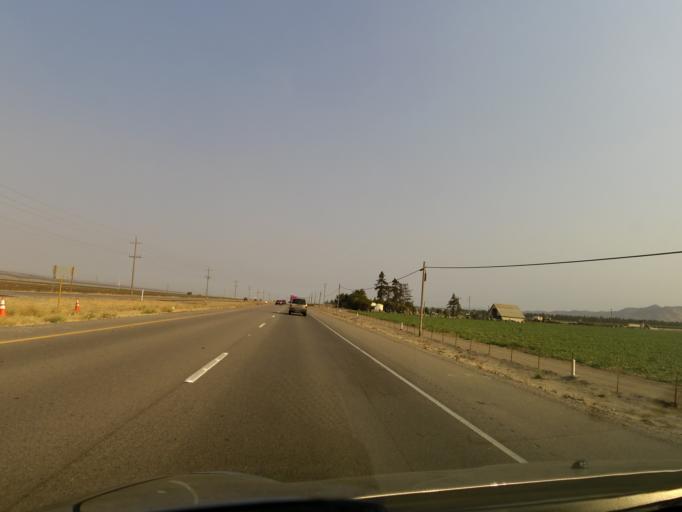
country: US
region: California
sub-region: Monterey County
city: Greenfield
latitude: 36.2870
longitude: -121.1941
